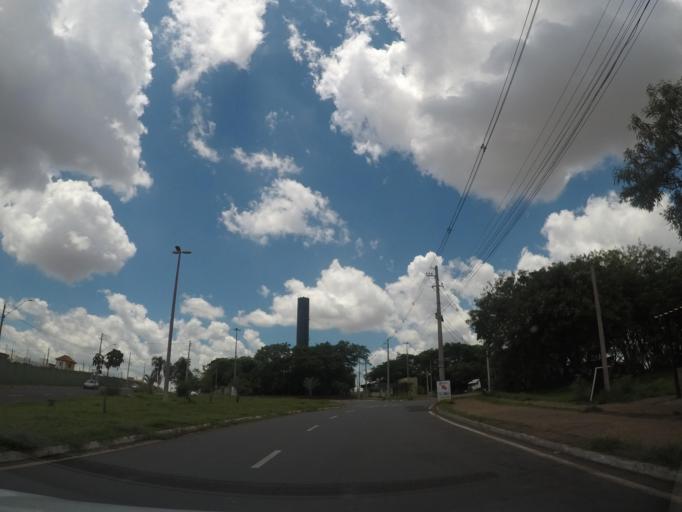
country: BR
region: Sao Paulo
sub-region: Hortolandia
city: Hortolandia
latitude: -22.8286
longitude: -47.2178
